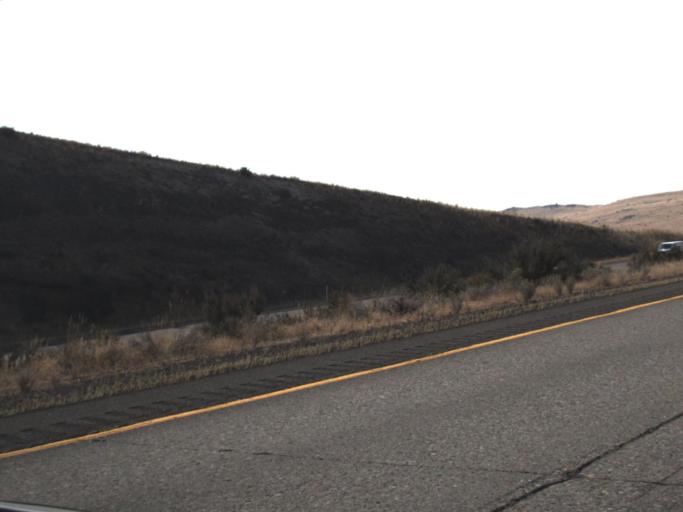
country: US
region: Washington
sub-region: Yakima County
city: Terrace Heights
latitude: 46.7312
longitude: -120.3861
